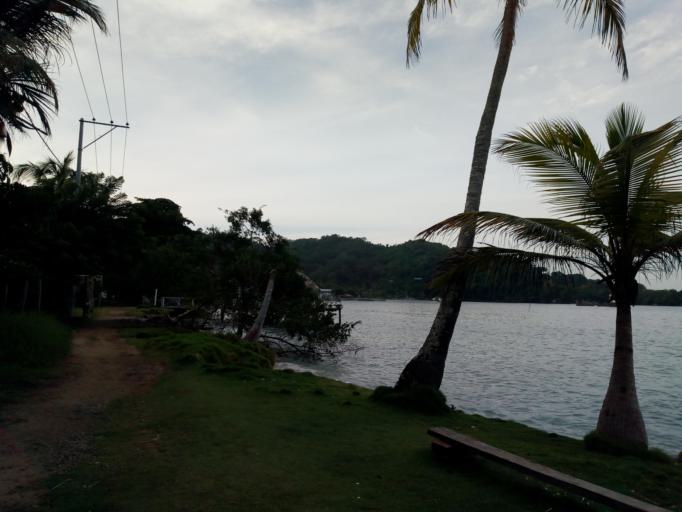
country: PA
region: Guna Yala
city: Puerto Obaldia
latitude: 8.6570
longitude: -77.3658
